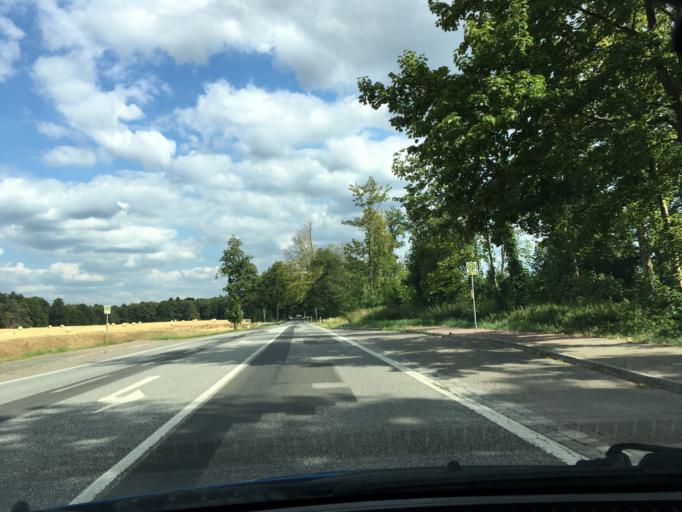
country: DE
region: Mecklenburg-Vorpommern
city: Lubtheen
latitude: 53.3916
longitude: 11.0549
